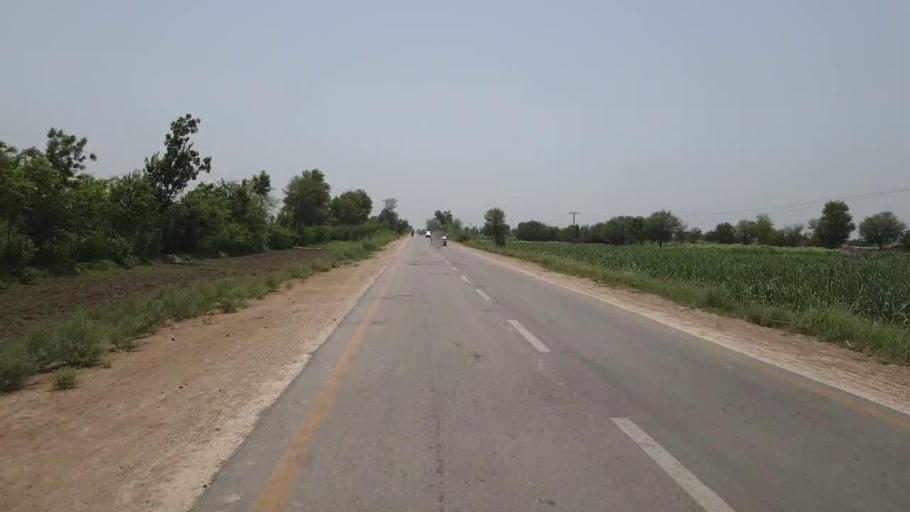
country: PK
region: Sindh
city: Moro
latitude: 26.5994
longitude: 68.0950
